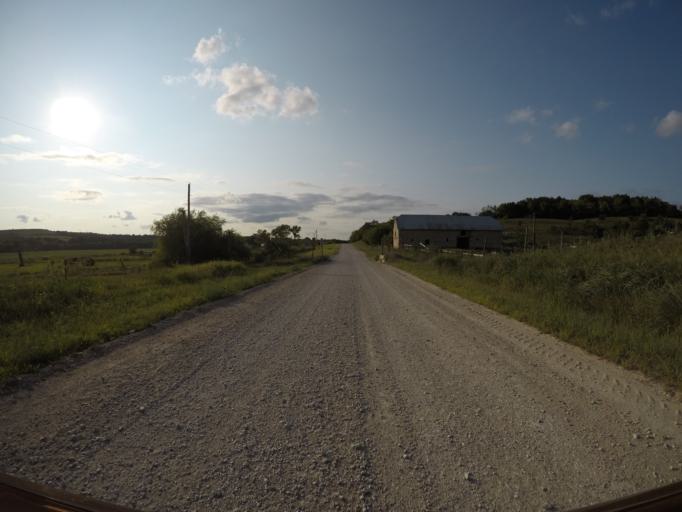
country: US
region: Kansas
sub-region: Wabaunsee County
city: Alma
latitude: 38.9441
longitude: -96.2383
